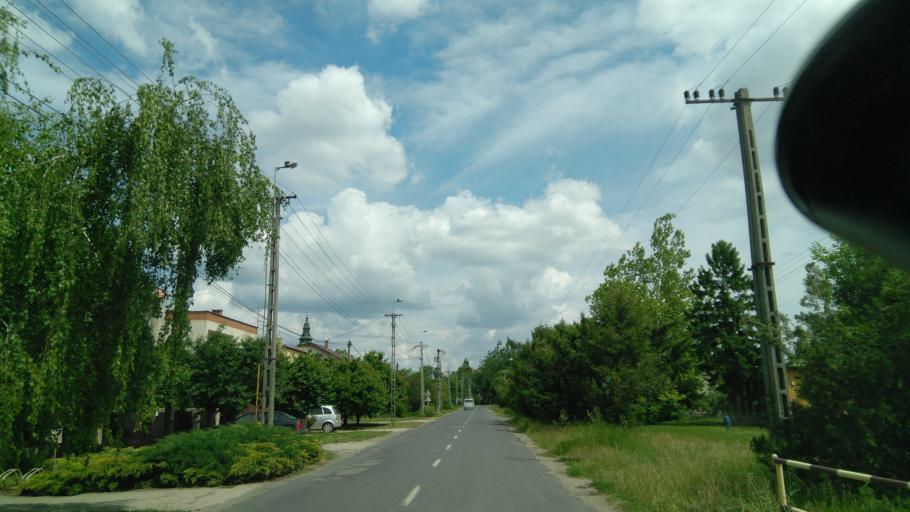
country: HU
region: Bekes
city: Totkomlos
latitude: 46.4116
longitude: 20.7316
